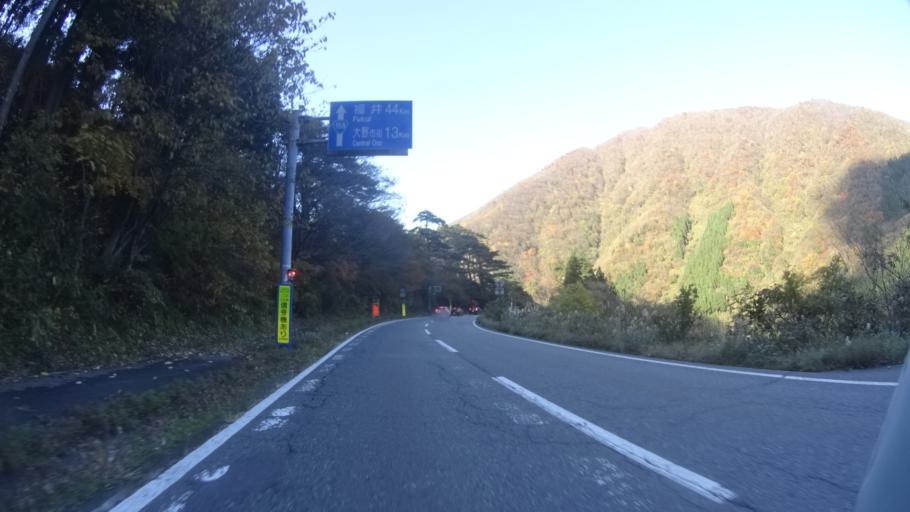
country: JP
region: Fukui
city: Ono
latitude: 35.9625
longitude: 136.6055
